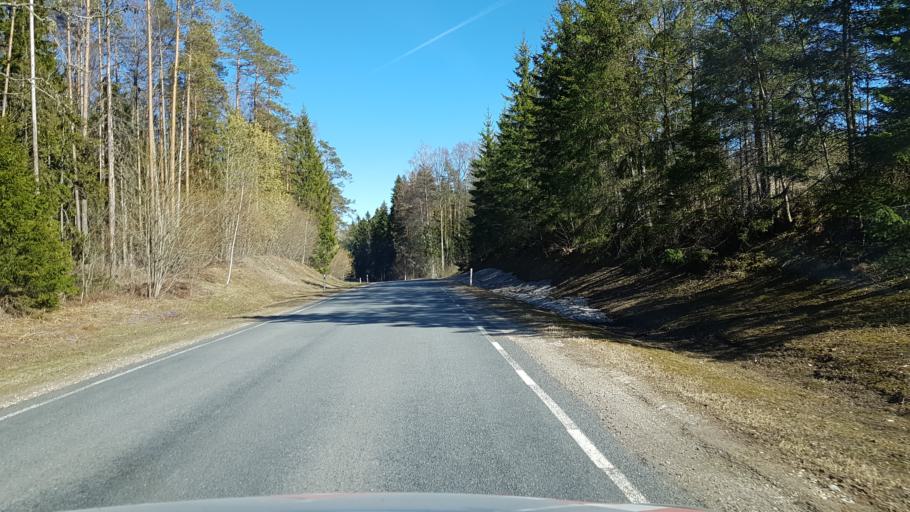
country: EE
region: Laeaene-Virumaa
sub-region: Vinni vald
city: Vinni
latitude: 59.2726
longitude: 26.6467
